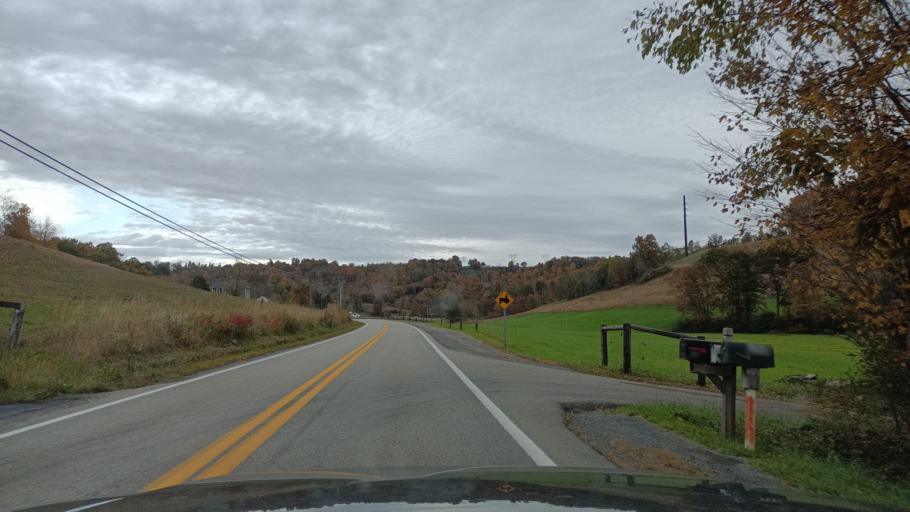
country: US
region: West Virginia
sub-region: Taylor County
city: Grafton
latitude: 39.3612
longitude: -79.9817
